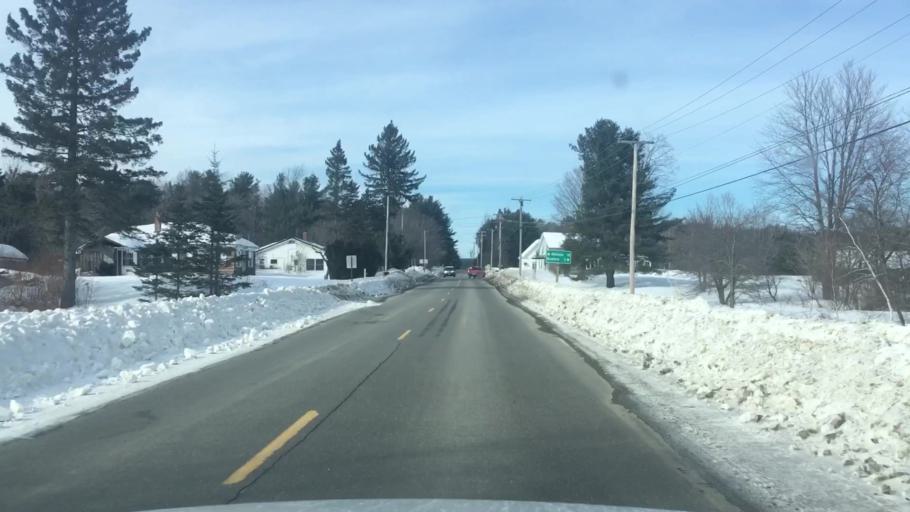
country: US
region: Maine
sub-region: Penobscot County
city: Charleston
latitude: 45.0513
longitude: -69.0301
